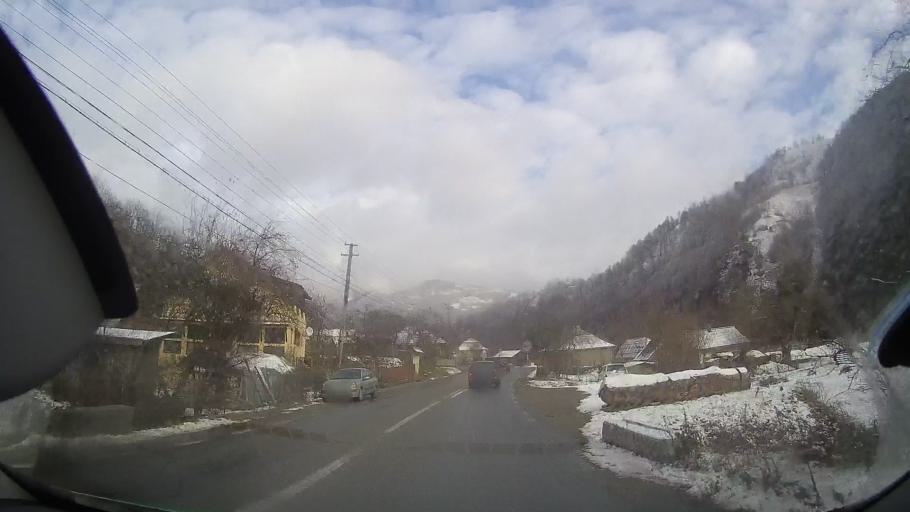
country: RO
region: Alba
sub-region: Oras Baia de Aries
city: Baia de Aries
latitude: 46.3912
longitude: 23.2991
